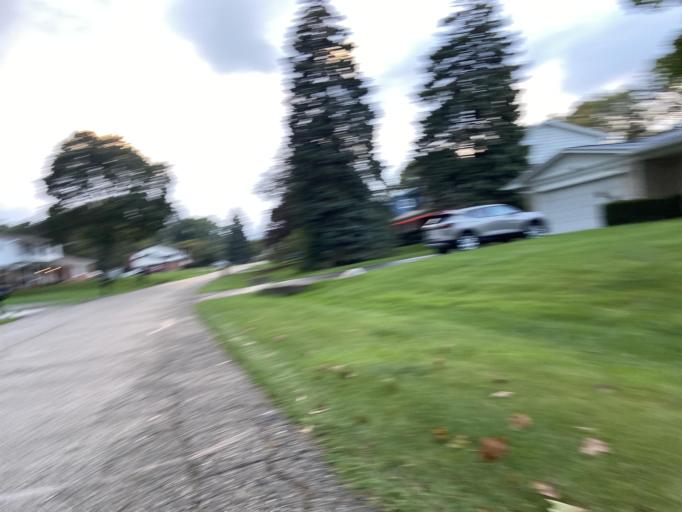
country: US
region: Michigan
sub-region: Oakland County
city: West Bloomfield Township
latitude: 42.5399
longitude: -83.3549
